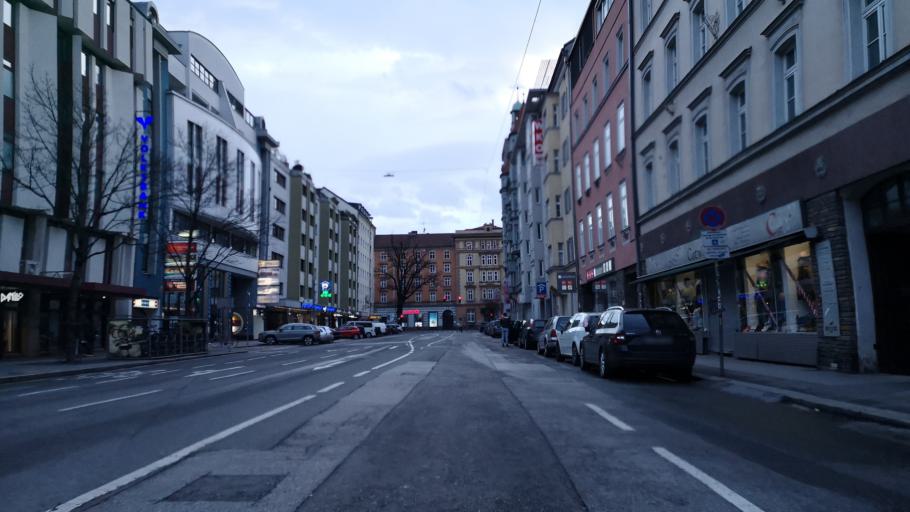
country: AT
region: Tyrol
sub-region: Innsbruck Stadt
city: Innsbruck
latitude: 47.2664
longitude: 11.3991
